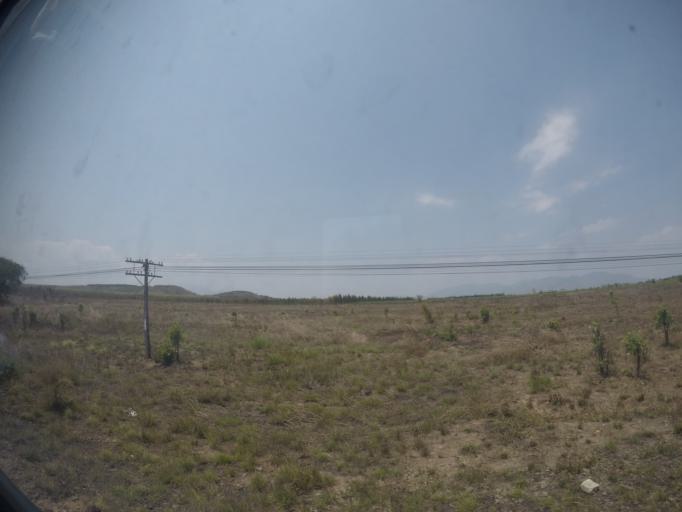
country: VN
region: Binh Thuan
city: Thuan Nam
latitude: 10.9302
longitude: 107.9383
